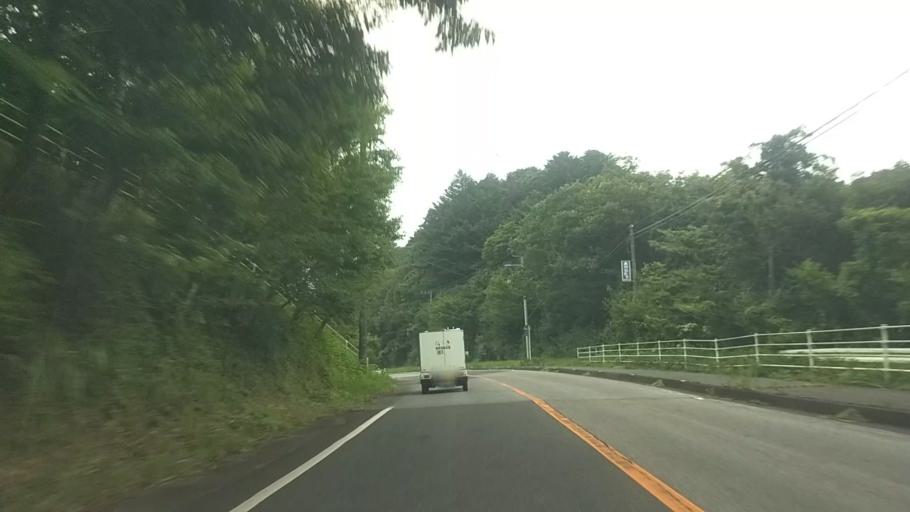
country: JP
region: Chiba
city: Kawaguchi
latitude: 35.1865
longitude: 140.0607
